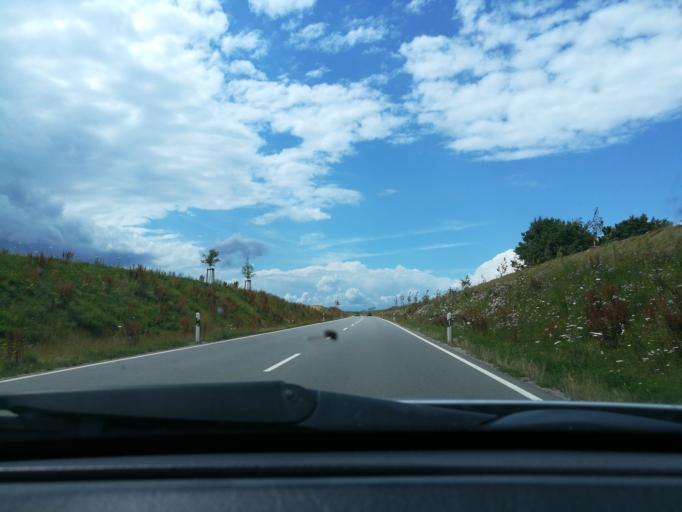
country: DE
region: Baden-Wuerttemberg
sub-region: Freiburg Region
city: Dunningen
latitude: 48.2126
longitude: 8.5323
